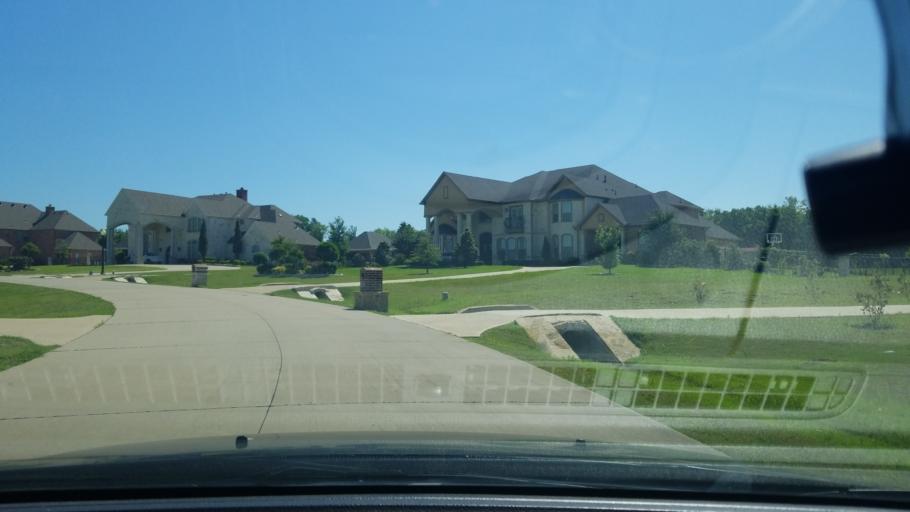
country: US
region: Texas
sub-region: Dallas County
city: Sunnyvale
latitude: 32.7969
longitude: -96.5668
